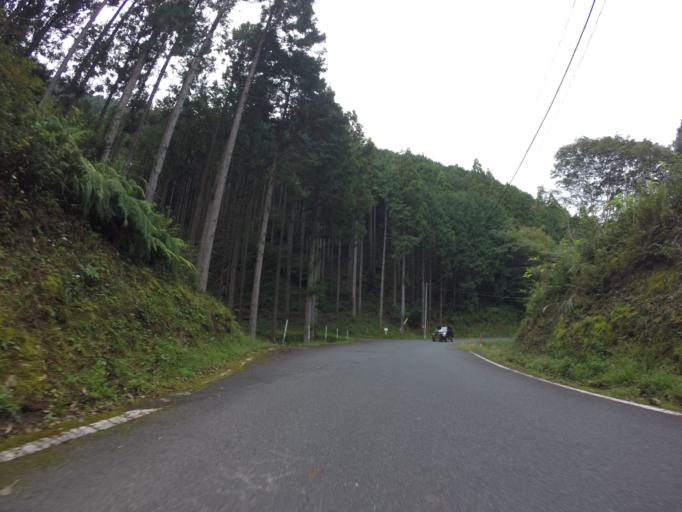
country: JP
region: Shizuoka
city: Mori
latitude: 34.8816
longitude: 138.0308
